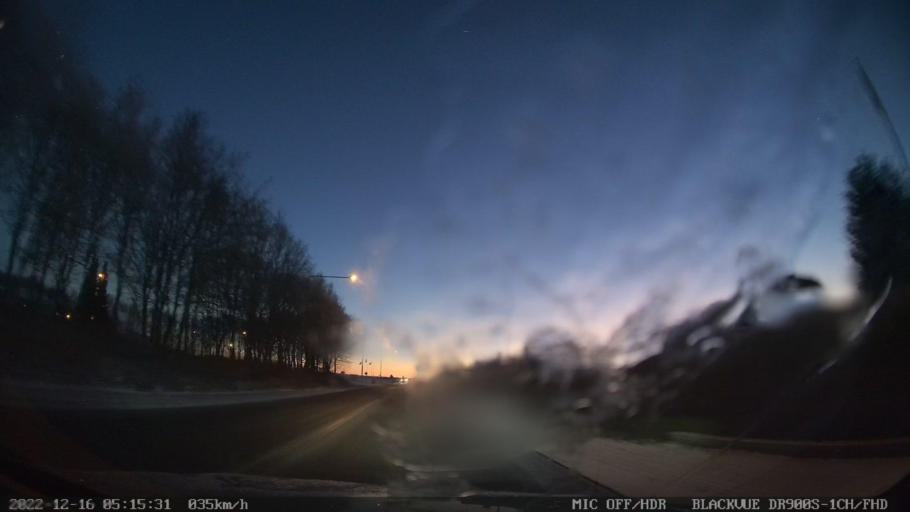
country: SE
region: Skane
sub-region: Tomelilla Kommun
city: Tomelilla
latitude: 55.5347
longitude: 13.9404
